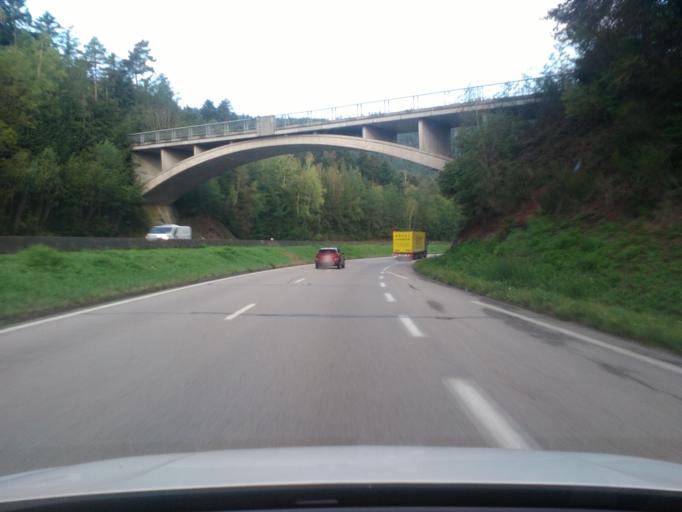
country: FR
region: Lorraine
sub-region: Departement des Vosges
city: Saint-Die-des-Vosges
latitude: 48.2640
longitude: 6.9447
